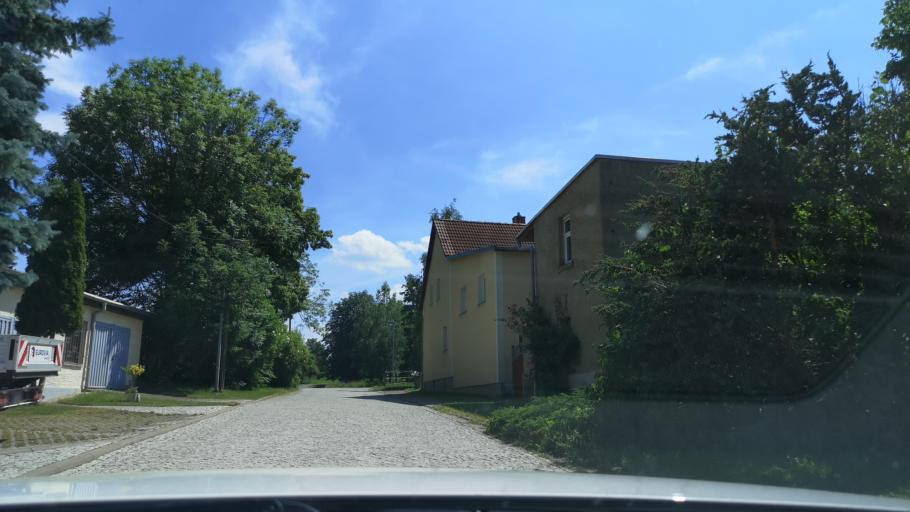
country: DE
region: Thuringia
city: Eberstedt
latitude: 51.0437
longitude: 11.5958
